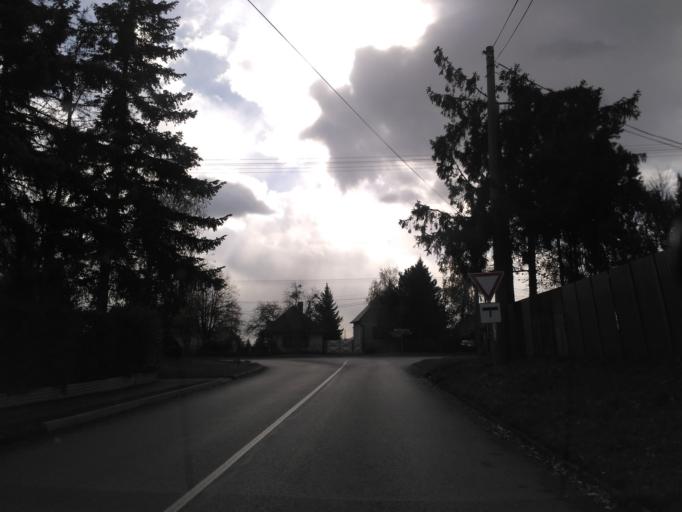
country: SK
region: Kosicky
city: Secovce
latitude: 48.7006
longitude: 21.6470
